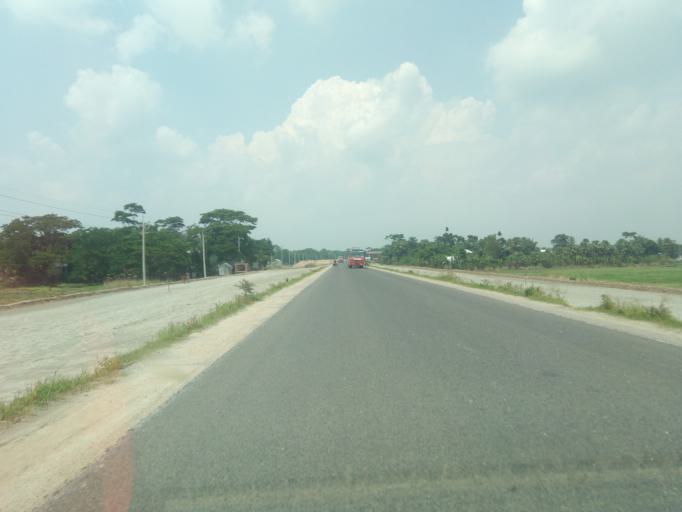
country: BD
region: Dhaka
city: Char Bhadrasan
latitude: 23.3873
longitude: 90.1258
